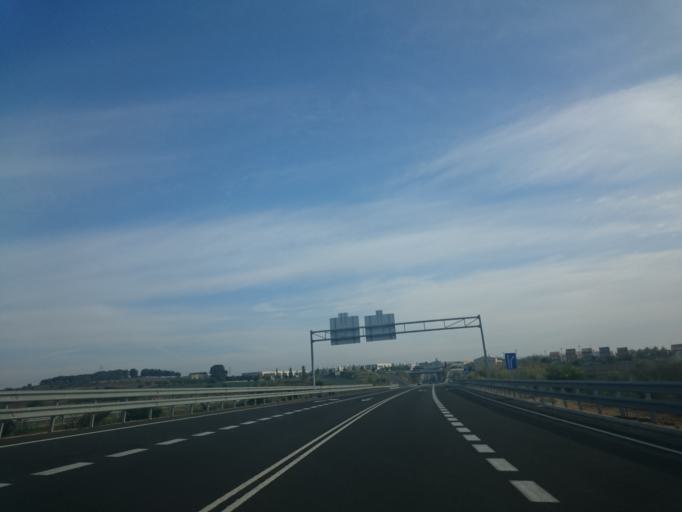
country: ES
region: Catalonia
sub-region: Provincia de Barcelona
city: La Granada
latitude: 41.3722
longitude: 1.7112
